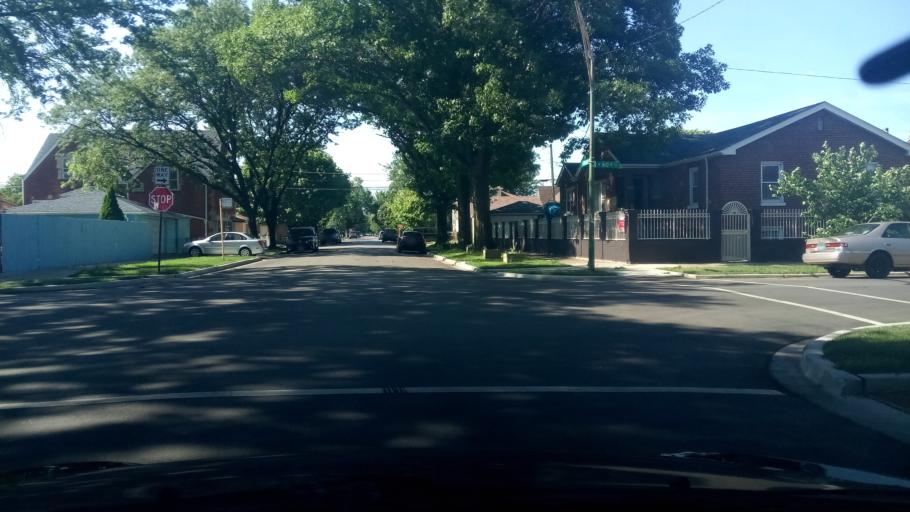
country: US
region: Illinois
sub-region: Cook County
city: Hometown
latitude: 41.7846
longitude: -87.7204
